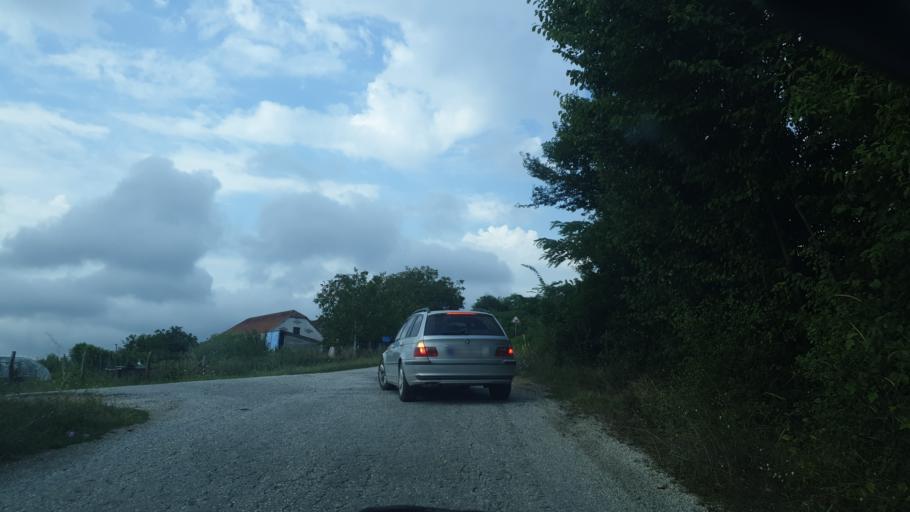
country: RS
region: Central Serbia
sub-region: Sumadijski Okrug
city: Kragujevac
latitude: 44.0985
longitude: 20.7797
